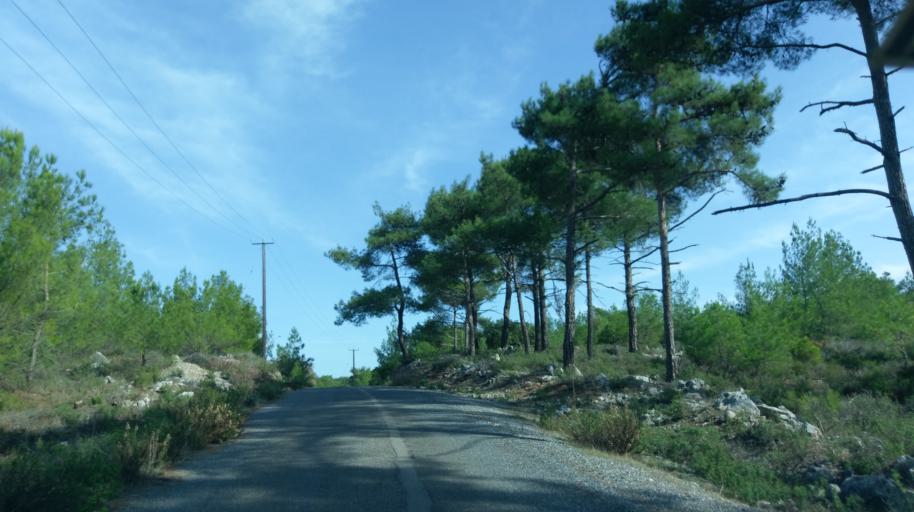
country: CY
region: Keryneia
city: Lapithos
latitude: 35.3066
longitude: 33.2446
